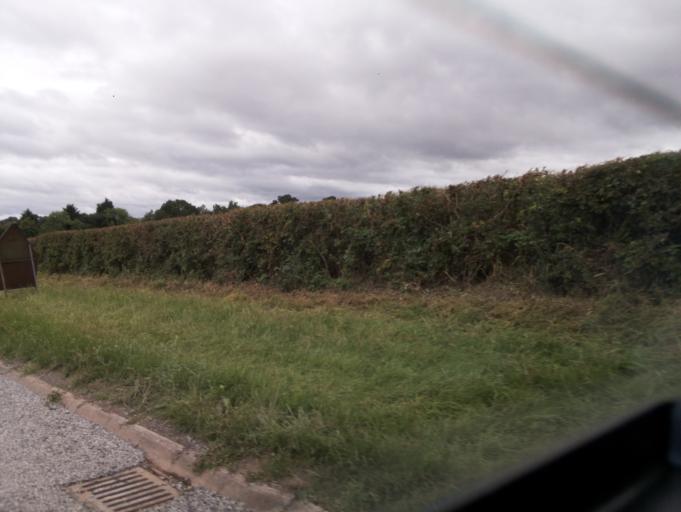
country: GB
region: England
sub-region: Worcestershire
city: Upton upon Severn
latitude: 52.0831
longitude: -2.2020
